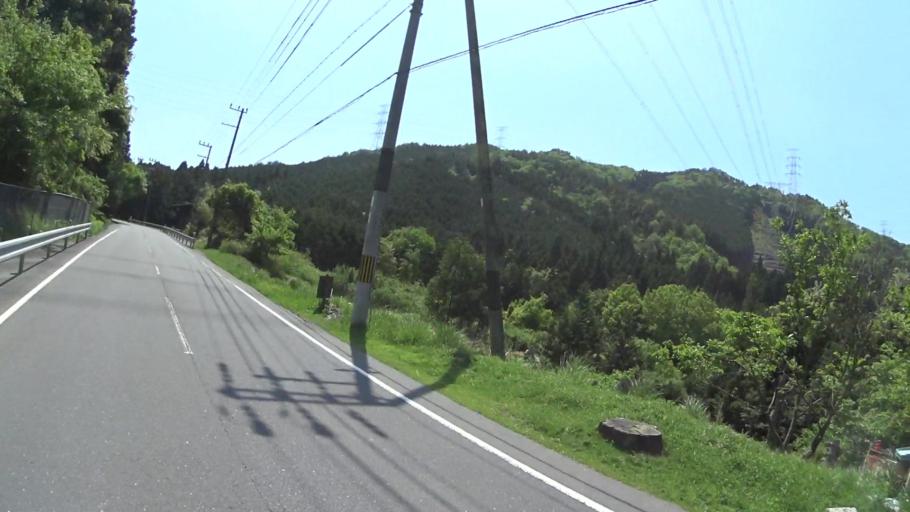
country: JP
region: Kyoto
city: Kameoka
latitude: 34.9979
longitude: 135.4783
